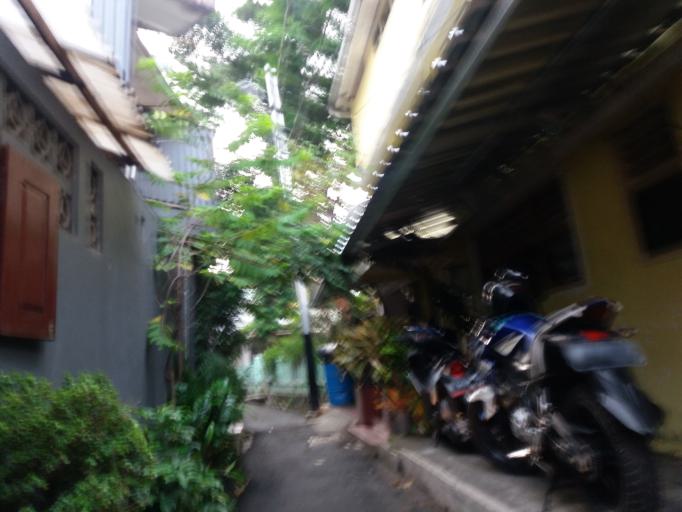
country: ID
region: Jakarta Raya
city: Jakarta
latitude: -6.2176
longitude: 106.8240
